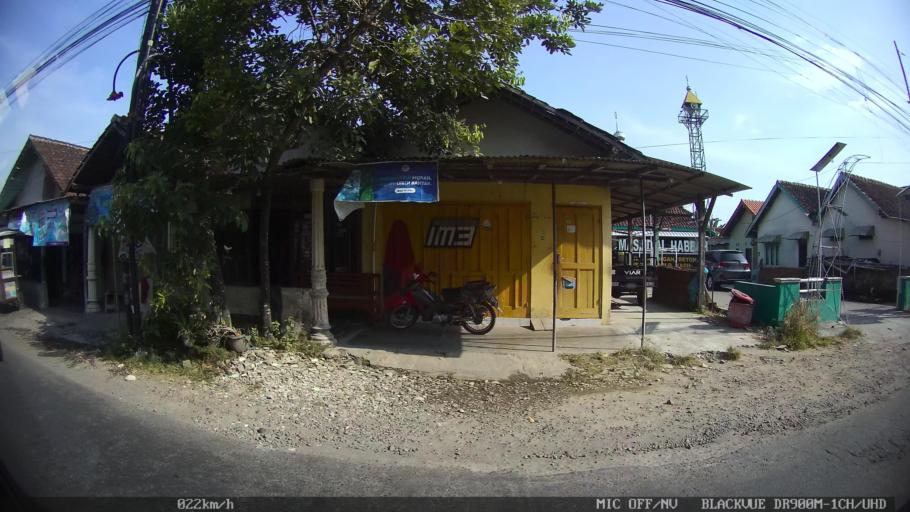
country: ID
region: Daerah Istimewa Yogyakarta
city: Kasihan
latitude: -7.8465
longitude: 110.3385
